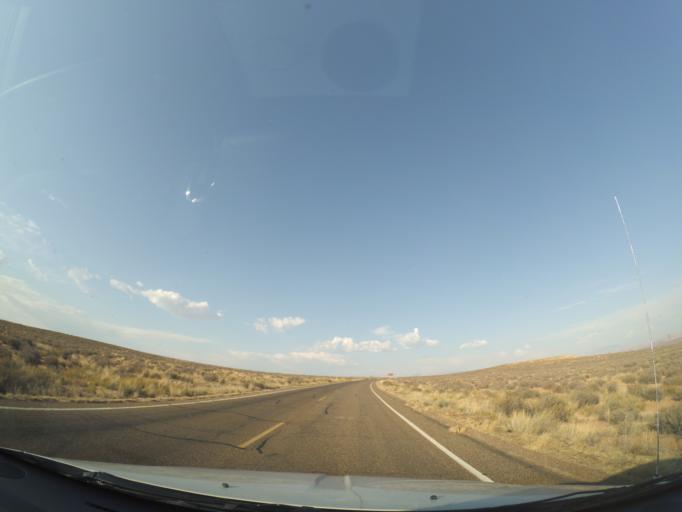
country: US
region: Arizona
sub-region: Coconino County
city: Page
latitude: 36.9843
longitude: -111.5247
